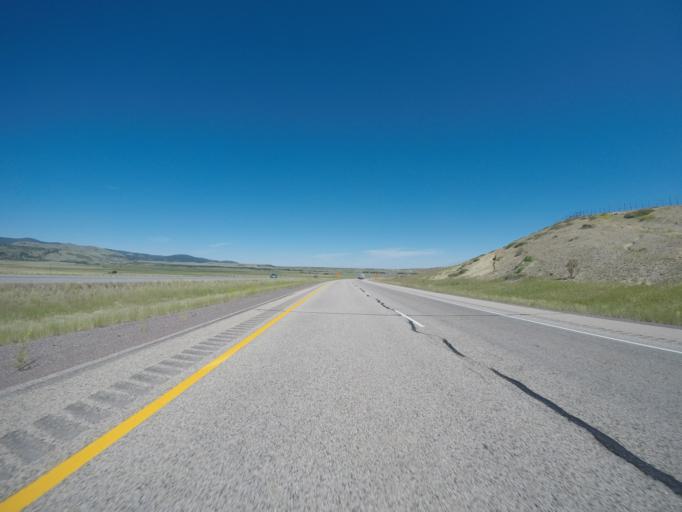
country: US
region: Wyoming
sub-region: Albany County
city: Laramie
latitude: 41.4974
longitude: -106.0470
